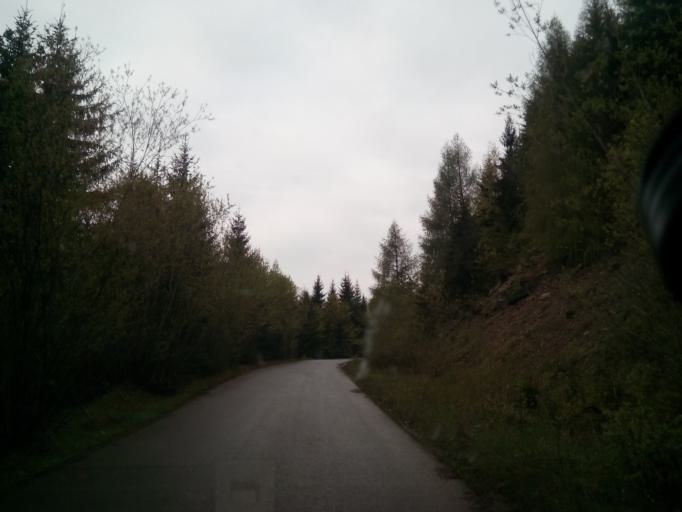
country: SK
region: Zilinsky
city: Oravska Lesna
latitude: 49.3082
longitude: 19.2066
